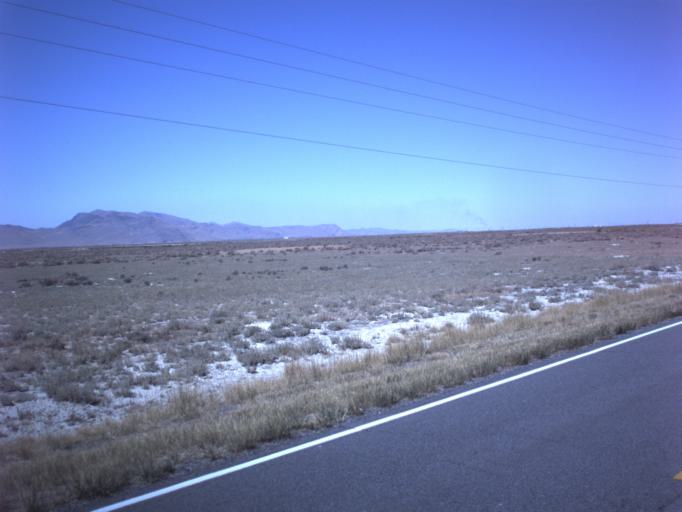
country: US
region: Utah
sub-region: Tooele County
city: Grantsville
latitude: 40.7223
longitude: -112.6597
